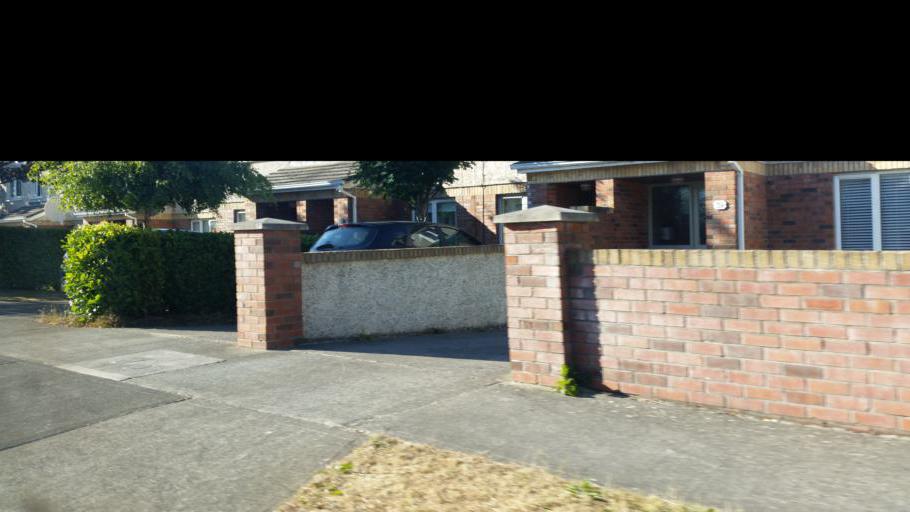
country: IE
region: Leinster
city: Hartstown
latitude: 53.3952
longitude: -6.4253
